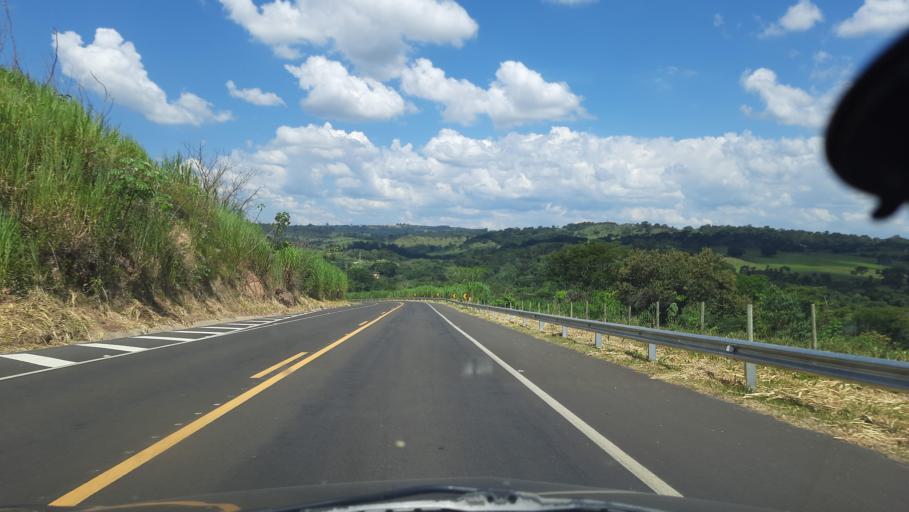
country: BR
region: Sao Paulo
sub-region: Sao Jose Do Rio Pardo
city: Sao Jose do Rio Pardo
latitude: -21.6033
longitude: -46.9766
